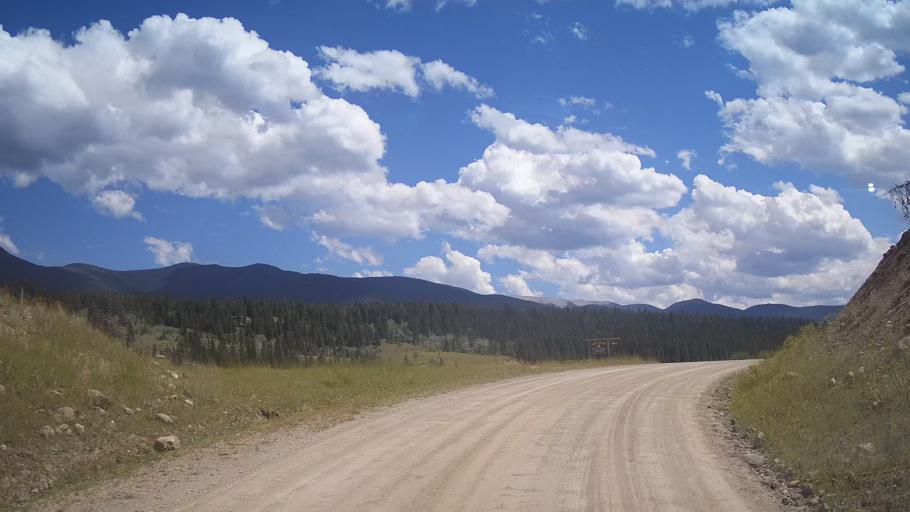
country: CA
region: British Columbia
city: Lillooet
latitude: 51.3026
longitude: -121.9837
